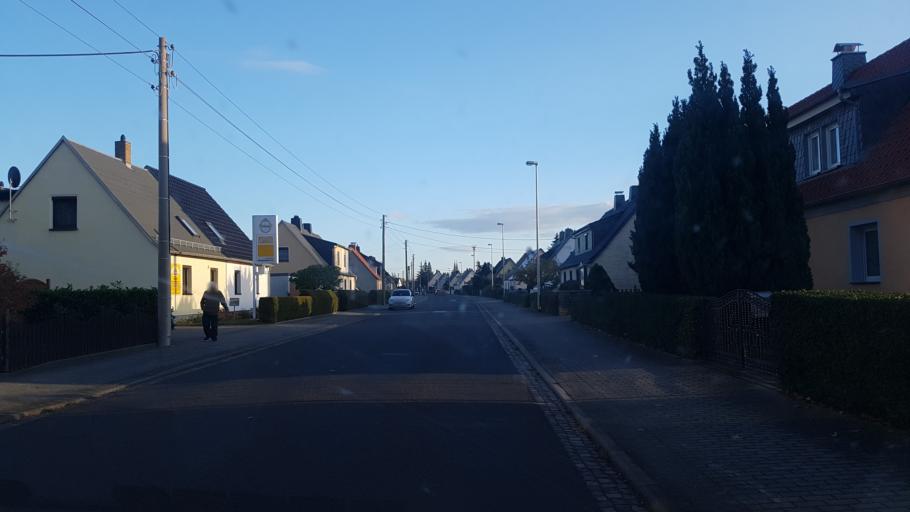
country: DE
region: Saxony
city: Oschatz
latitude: 51.3078
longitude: 13.0969
